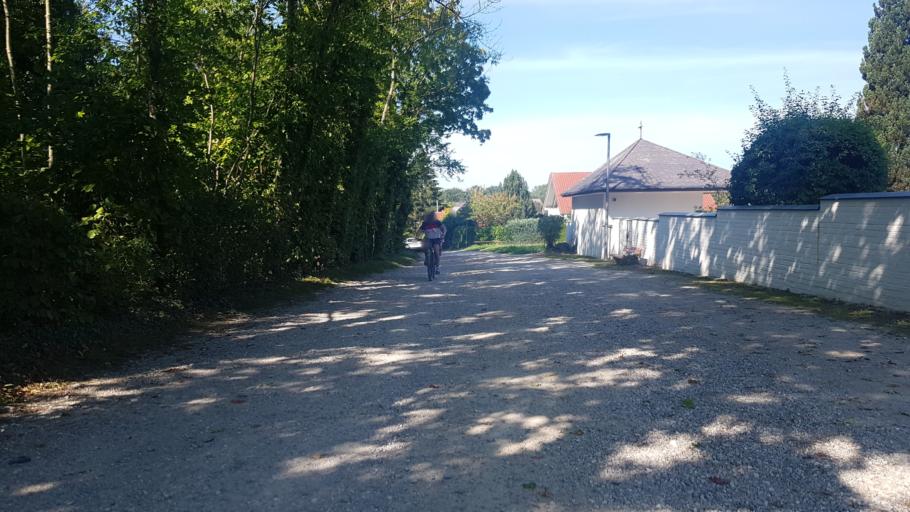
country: DE
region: Bavaria
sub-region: Upper Bavaria
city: Inning am Ammersee
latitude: 48.0372
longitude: 11.1374
